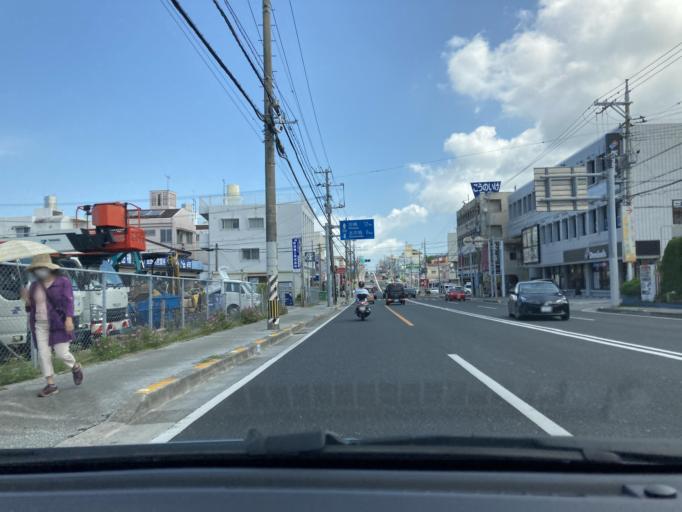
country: JP
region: Okinawa
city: Ginowan
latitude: 26.2639
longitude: 127.7628
